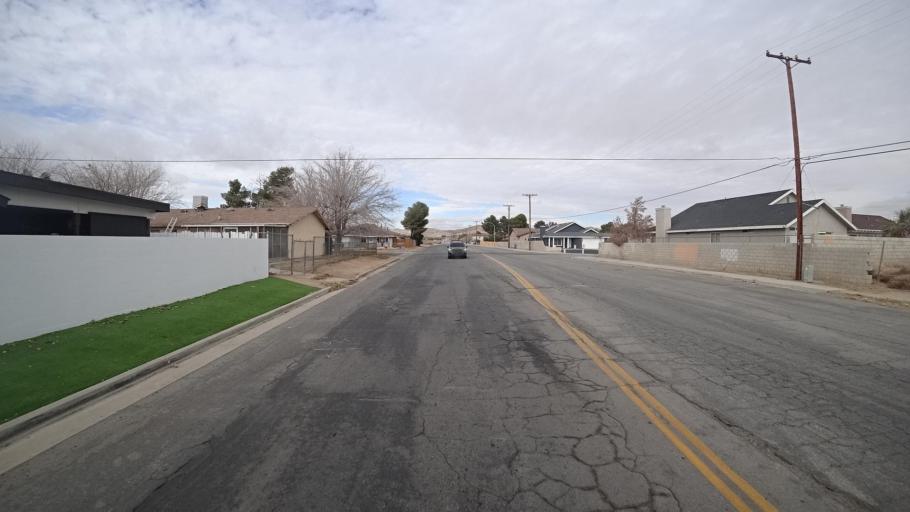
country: US
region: California
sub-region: Kern County
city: Rosamond
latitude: 34.8665
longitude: -118.1583
